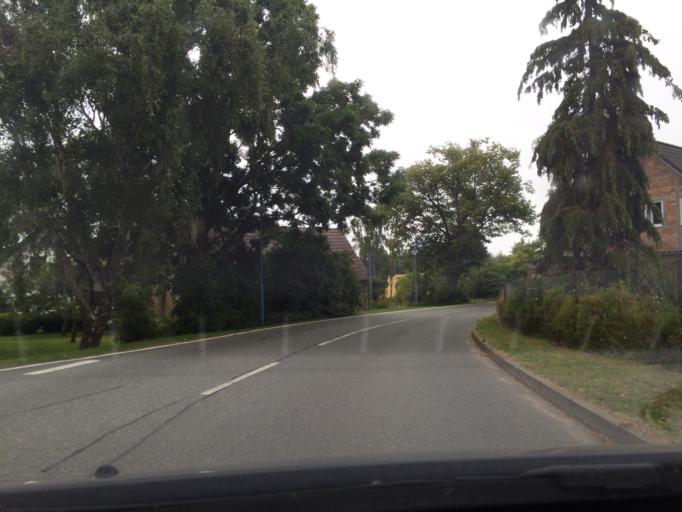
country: DE
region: Mecklenburg-Vorpommern
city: Prohn
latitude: 54.4157
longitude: 13.0136
